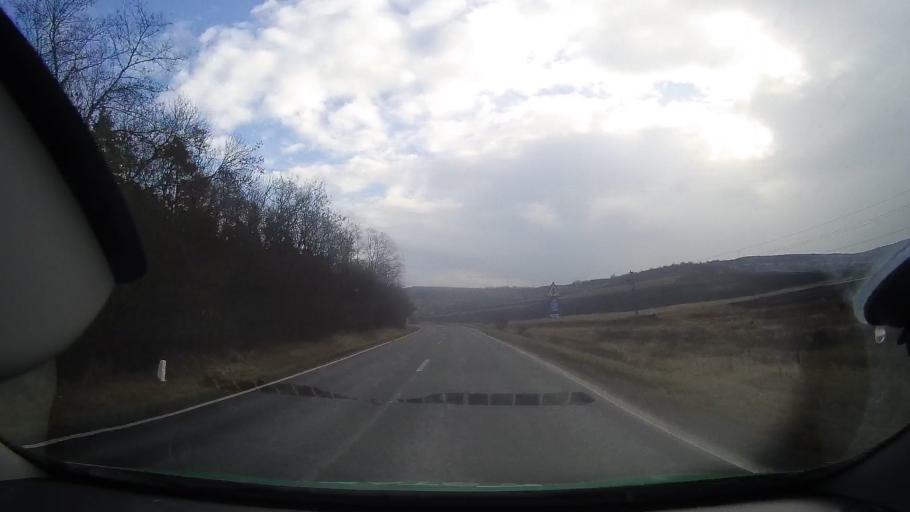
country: RO
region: Mures
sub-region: Comuna Cucerdea
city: Cucerdea
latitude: 46.3661
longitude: 24.2661
